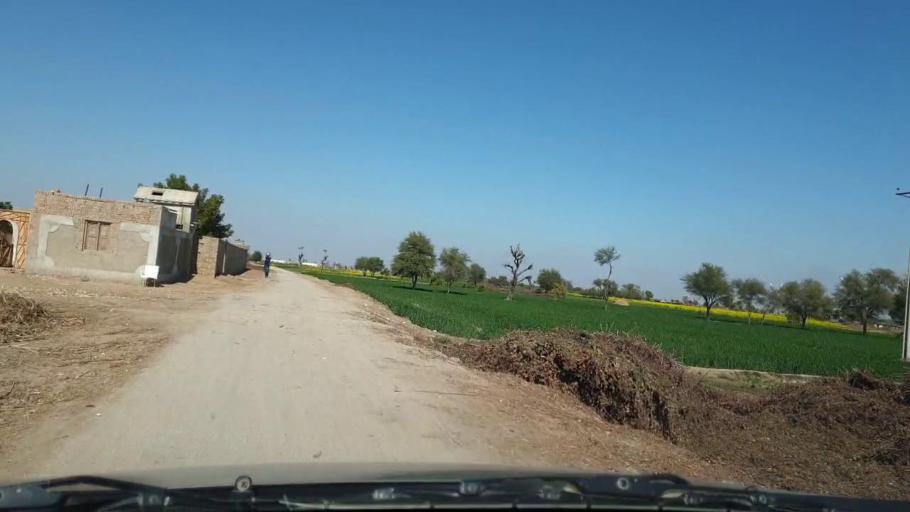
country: PK
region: Sindh
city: Khadro
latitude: 26.1444
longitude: 68.7951
